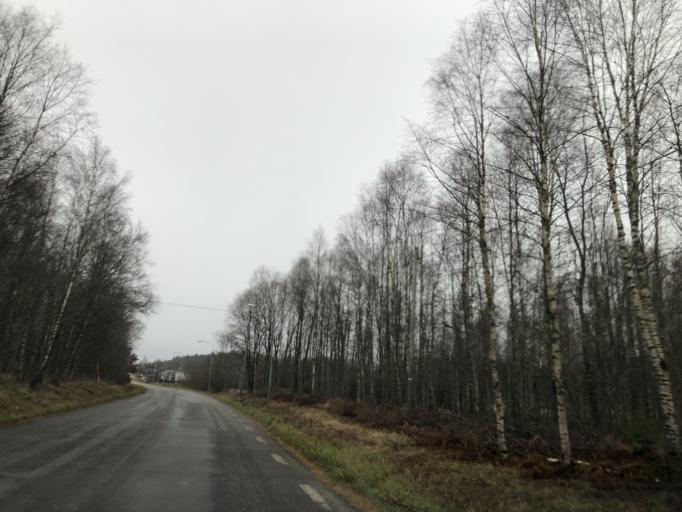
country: SE
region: Vaestra Goetaland
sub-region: Ulricehamns Kommun
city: Ulricehamn
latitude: 57.6959
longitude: 13.4940
